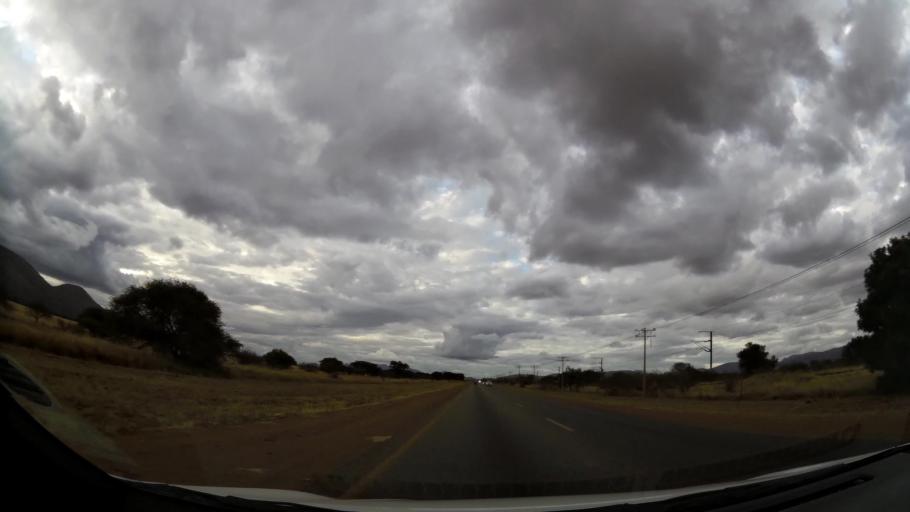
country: ZA
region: Limpopo
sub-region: Waterberg District Municipality
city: Mokopane
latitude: -24.2560
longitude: 28.9879
